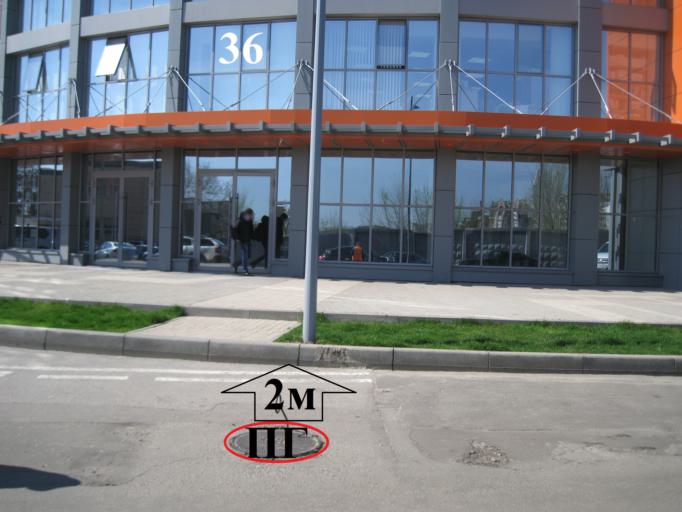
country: RU
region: Voronezj
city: Voronezh
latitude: 51.6553
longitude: 39.1945
